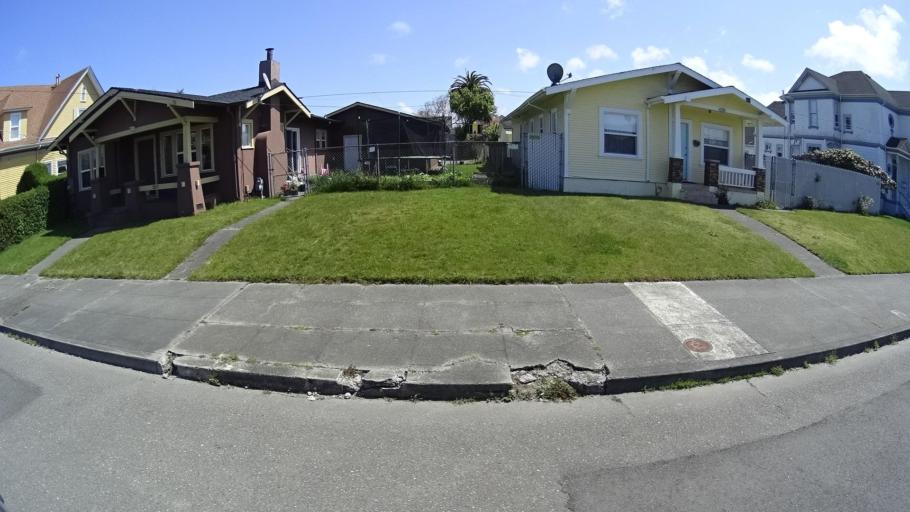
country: US
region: California
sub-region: Humboldt County
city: Bayview
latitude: 40.7822
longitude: -124.1720
